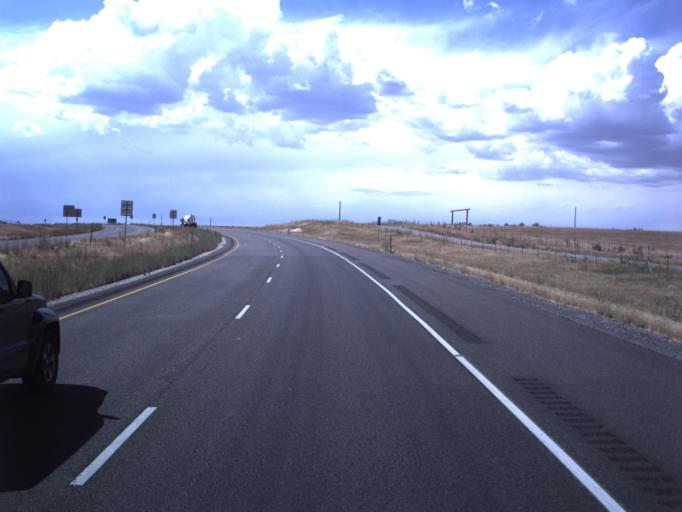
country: US
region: Idaho
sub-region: Oneida County
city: Malad City
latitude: 41.9044
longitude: -112.5829
